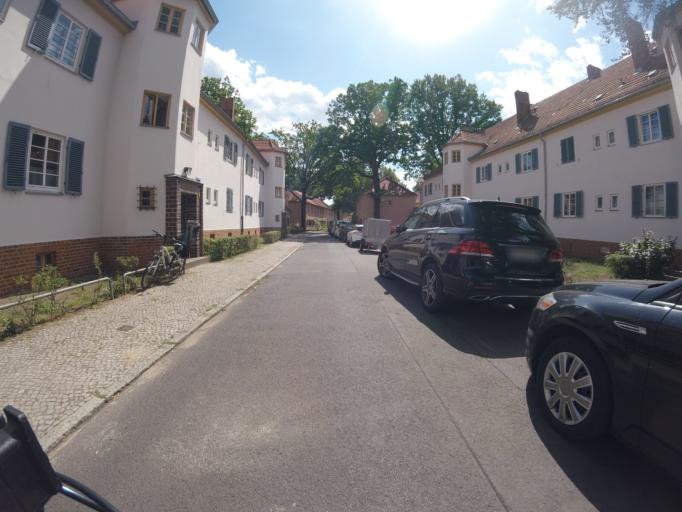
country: DE
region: Berlin
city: Siemensstadt
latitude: 52.5456
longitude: 13.2622
